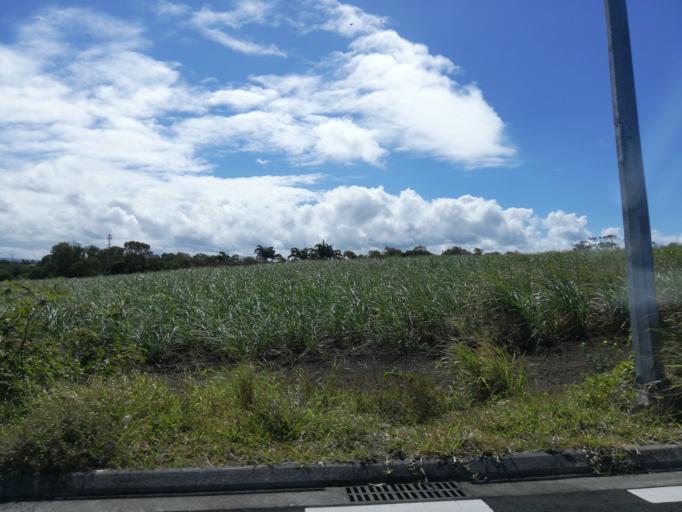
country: MU
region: Grand Port
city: Beau Vallon
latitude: -20.4499
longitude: 57.6960
